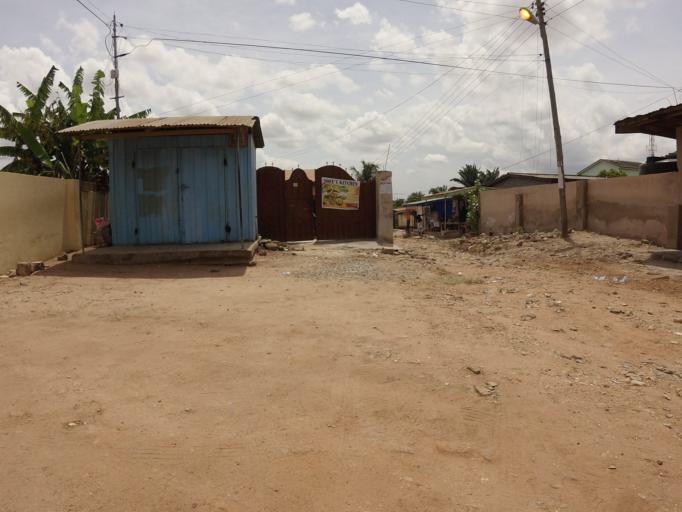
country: GH
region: Greater Accra
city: Dome
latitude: 5.6135
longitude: -0.2422
